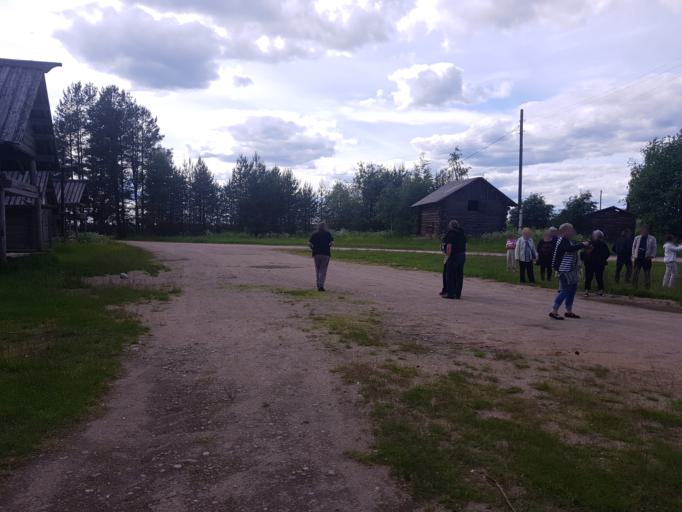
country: RU
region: Republic of Karelia
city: Kostomuksha
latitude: 64.9545
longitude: 30.5578
